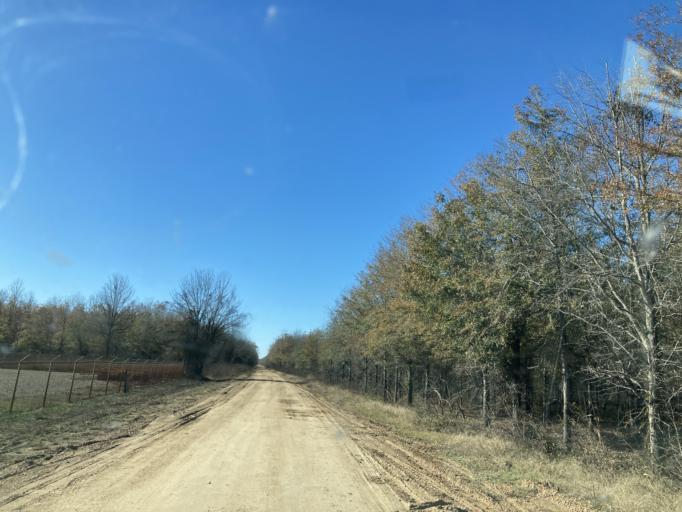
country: US
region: Mississippi
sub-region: Sharkey County
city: Rolling Fork
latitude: 32.7491
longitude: -90.6629
